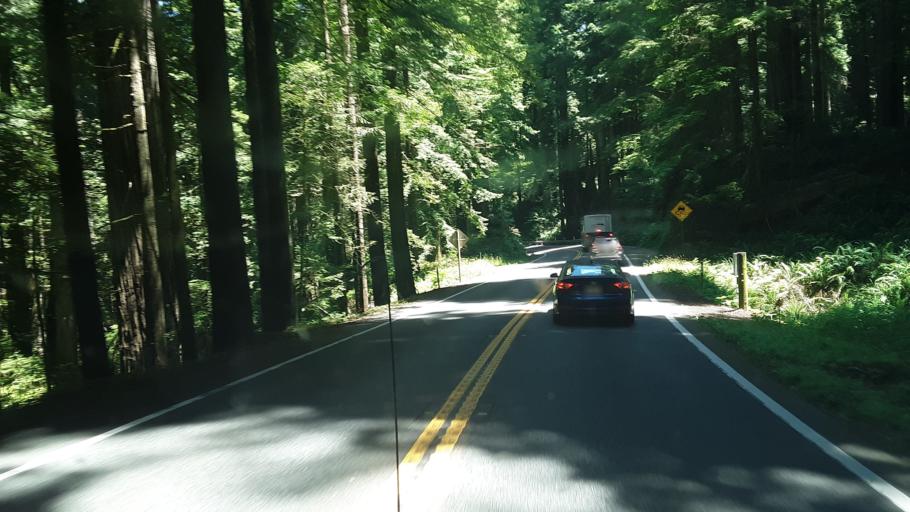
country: US
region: California
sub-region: Del Norte County
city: Bertsch-Oceanview
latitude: 41.8107
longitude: -124.1274
